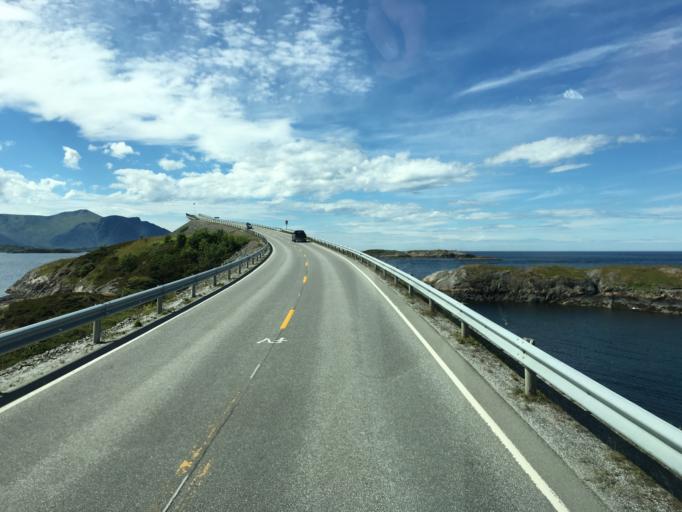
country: NO
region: More og Romsdal
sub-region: Eide
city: Eide
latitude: 63.0179
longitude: 7.3614
